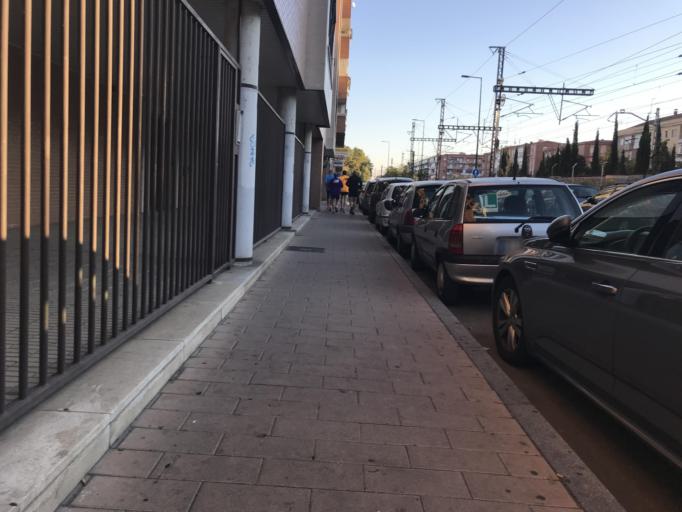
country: ES
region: Castille and Leon
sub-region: Provincia de Valladolid
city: Valladolid
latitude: 41.6492
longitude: -4.7122
